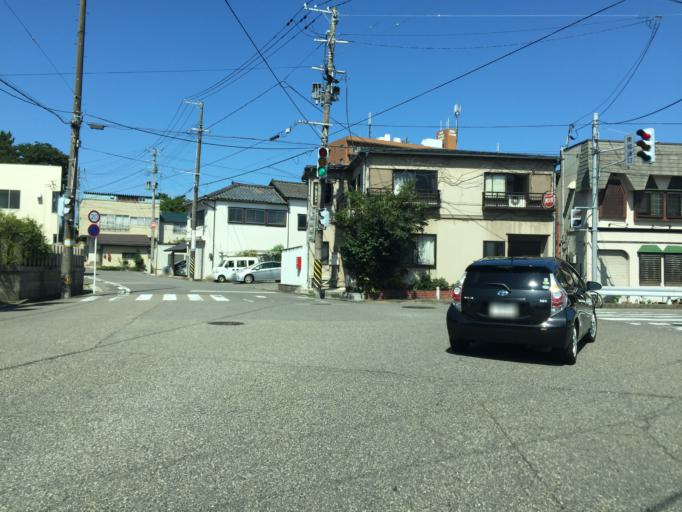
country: JP
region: Niigata
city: Niigata-shi
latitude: 37.9309
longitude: 139.0472
